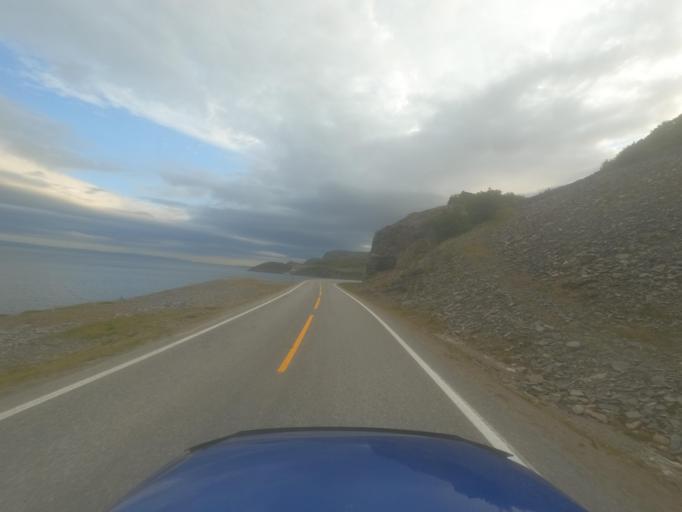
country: NO
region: Finnmark Fylke
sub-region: Nordkapp
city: Honningsvag
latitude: 70.6482
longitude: 25.3849
